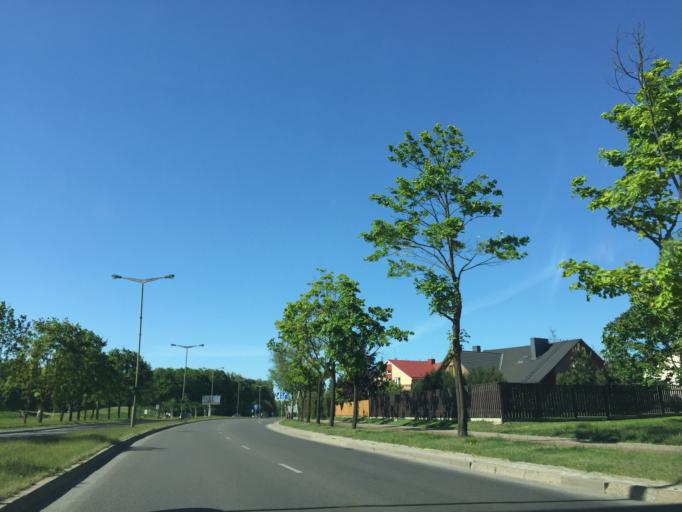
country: LT
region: Panevezys
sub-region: Panevezys City
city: Panevezys
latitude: 55.7371
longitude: 24.3389
